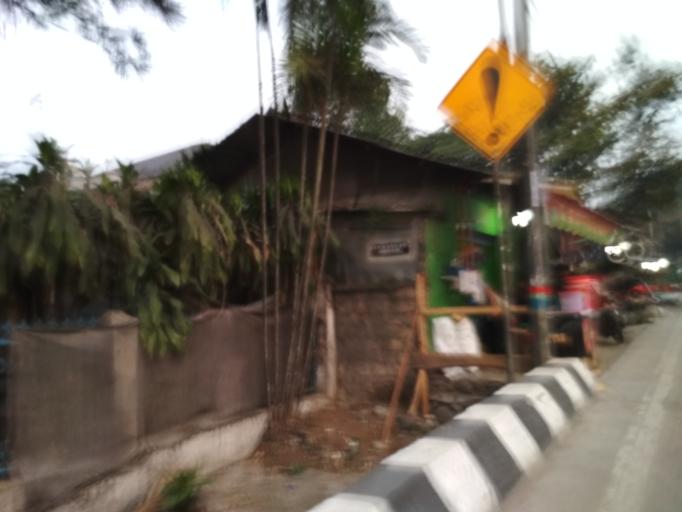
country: ID
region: West Java
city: Caringin
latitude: -6.6704
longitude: 106.8468
